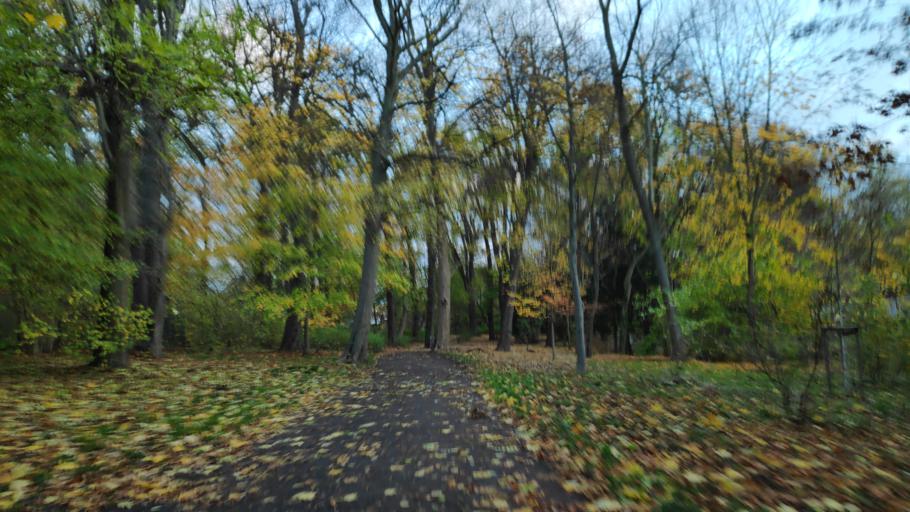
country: DE
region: North Rhine-Westphalia
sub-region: Regierungsbezirk Detmold
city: Minden
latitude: 52.2834
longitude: 8.9167
